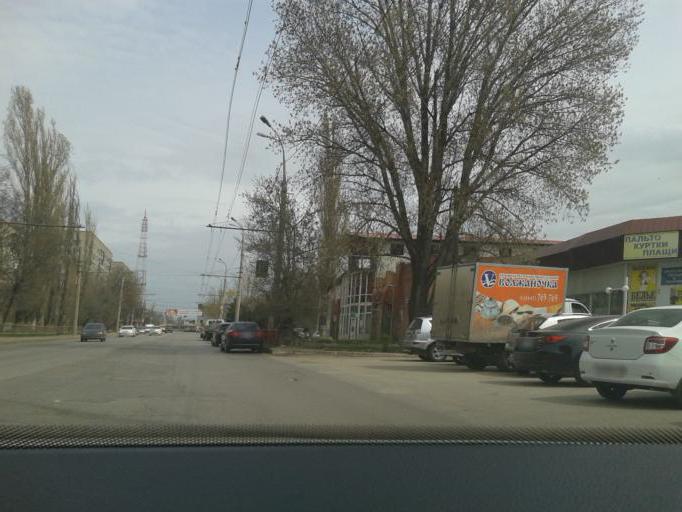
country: RU
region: Volgograd
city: Volgograd
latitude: 48.7363
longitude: 44.4988
